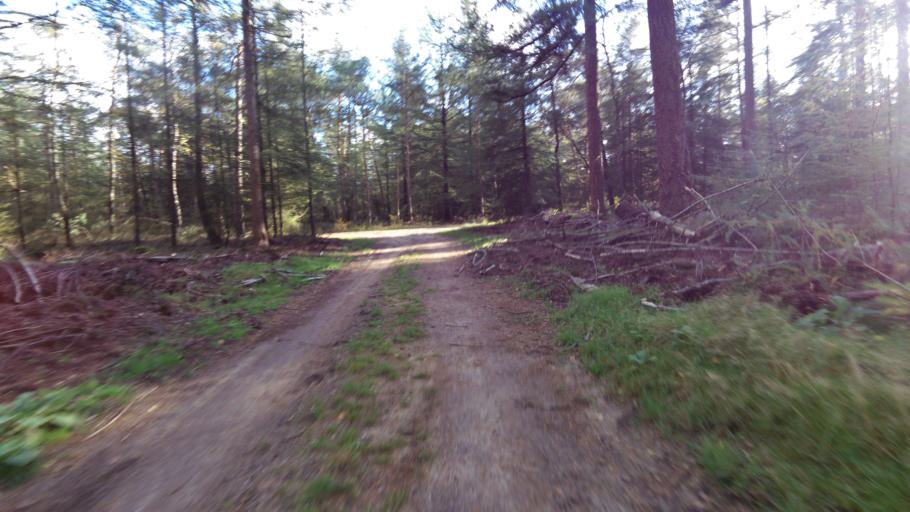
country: NL
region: Gelderland
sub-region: Gemeente Nunspeet
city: Nunspeet
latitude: 52.3454
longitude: 5.8520
